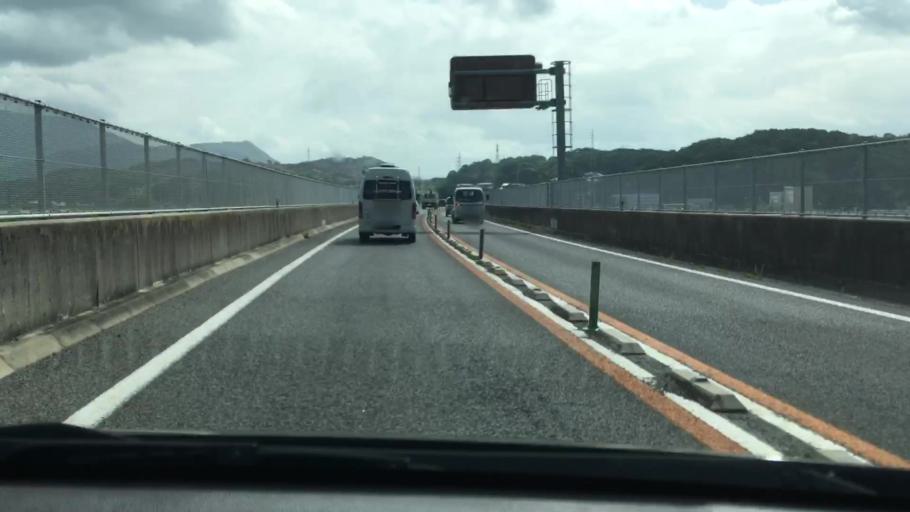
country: JP
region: Nagasaki
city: Sasebo
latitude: 33.1508
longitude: 129.7452
